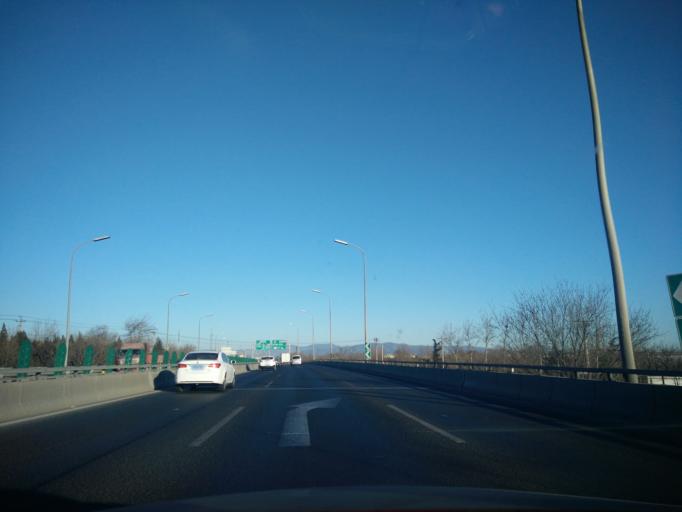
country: CN
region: Beijing
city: Fengtai
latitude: 39.8364
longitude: 116.2269
